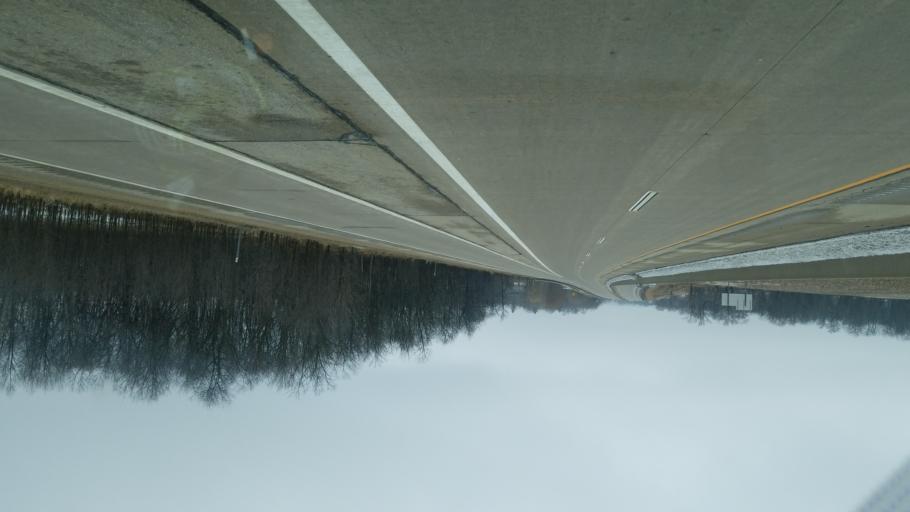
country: US
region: Wisconsin
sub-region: Waupaca County
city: Weyauwega
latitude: 44.2539
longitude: -88.8543
